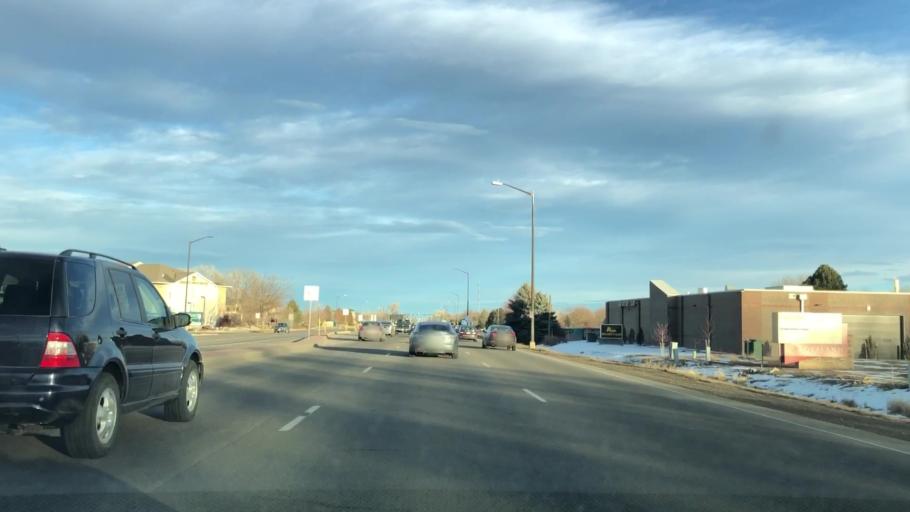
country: US
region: Colorado
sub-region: Larimer County
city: Loveland
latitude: 40.4072
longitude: -105.0522
